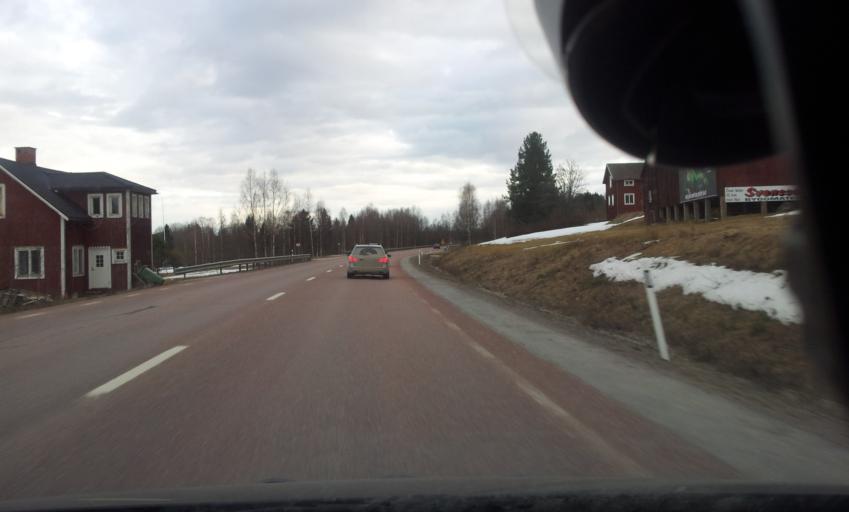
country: SE
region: Gaevleborg
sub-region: Ljusdals Kommun
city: Jaervsoe
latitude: 61.7268
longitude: 16.1682
